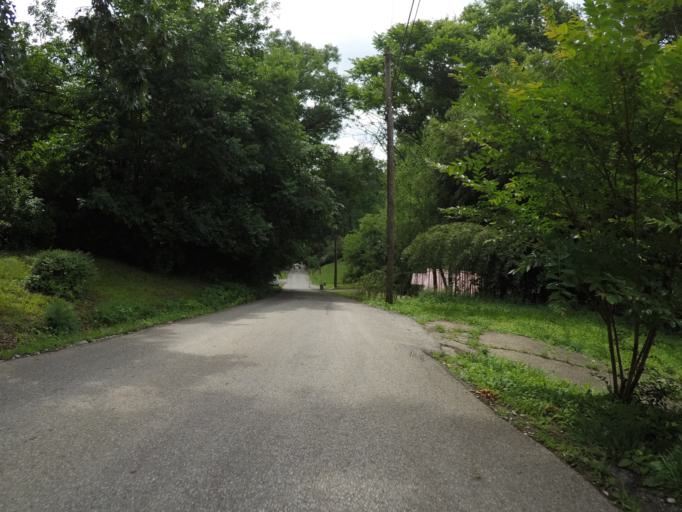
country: US
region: West Virginia
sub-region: Cabell County
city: Huntington
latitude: 38.4125
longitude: -82.3955
